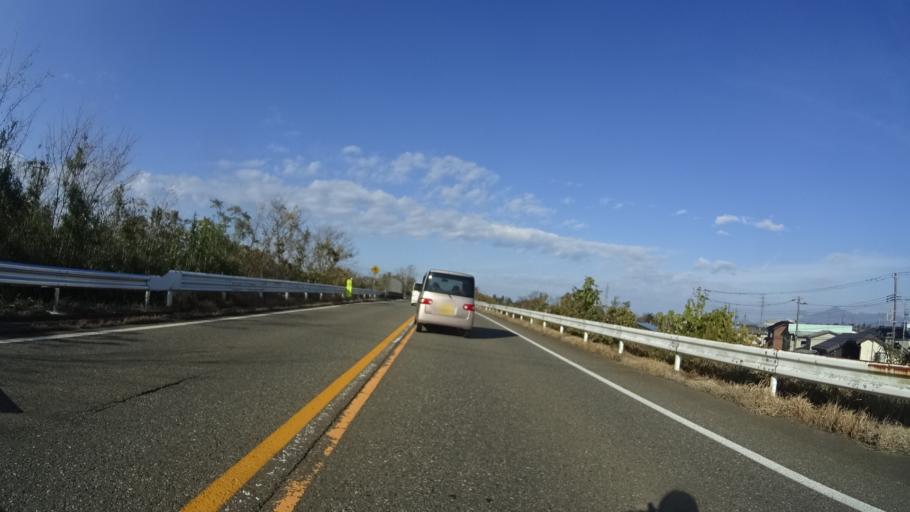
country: JP
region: Niigata
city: Joetsu
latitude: 37.2064
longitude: 138.3002
